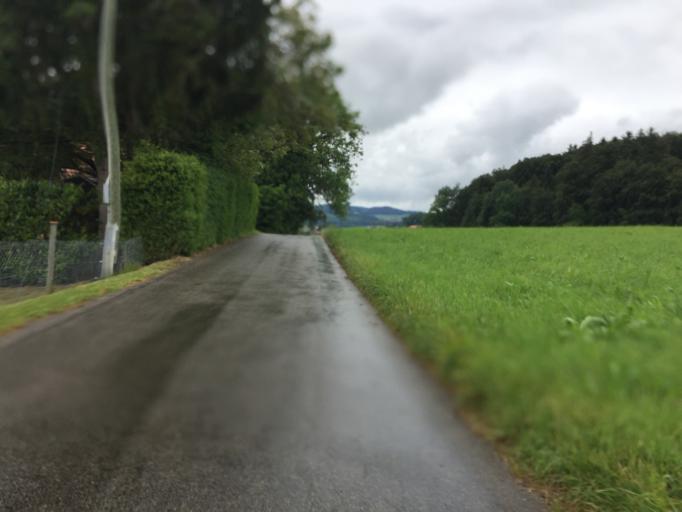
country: CH
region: Bern
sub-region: Bern-Mittelland District
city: Taegertschi
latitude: 46.8933
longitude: 7.5785
